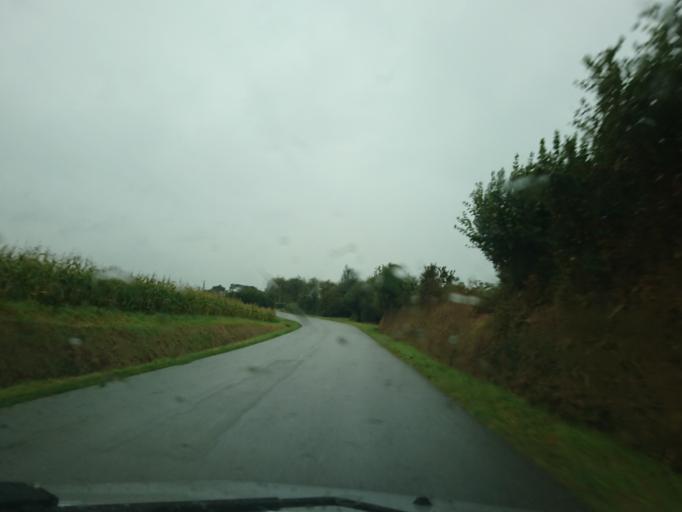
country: FR
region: Brittany
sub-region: Departement du Finistere
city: Kernilis
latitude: 48.5463
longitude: -4.4102
